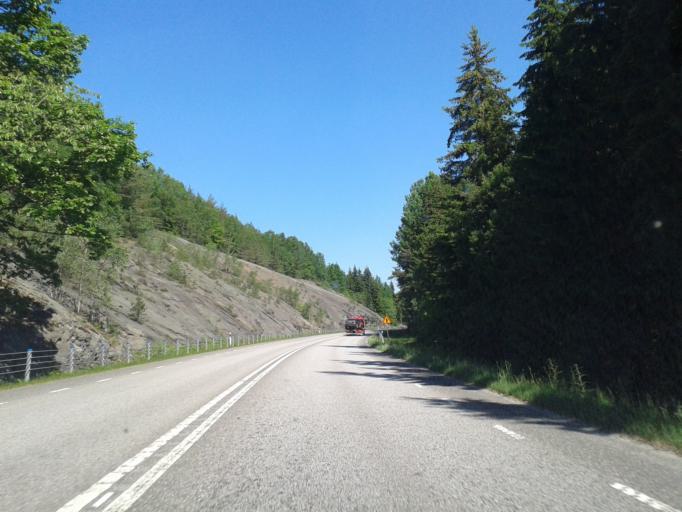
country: SE
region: Vaestra Goetaland
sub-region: Orust
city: Henan
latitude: 58.1921
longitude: 11.6889
